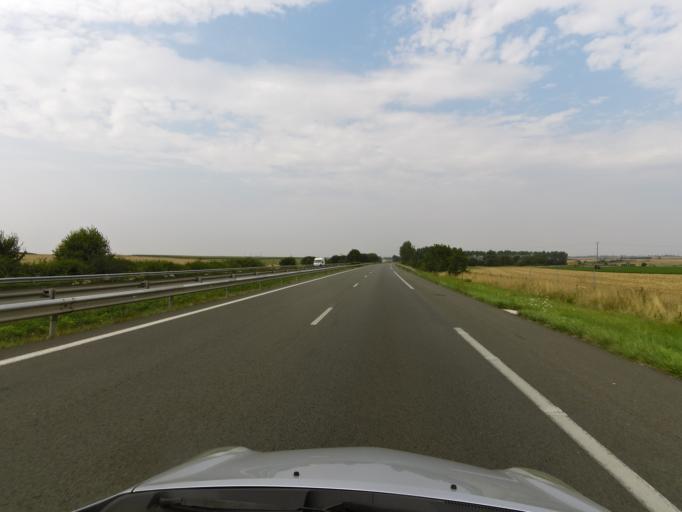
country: FR
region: Nord-Pas-de-Calais
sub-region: Departement du Pas-de-Calais
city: Bourlon
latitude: 50.1771
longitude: 3.1008
